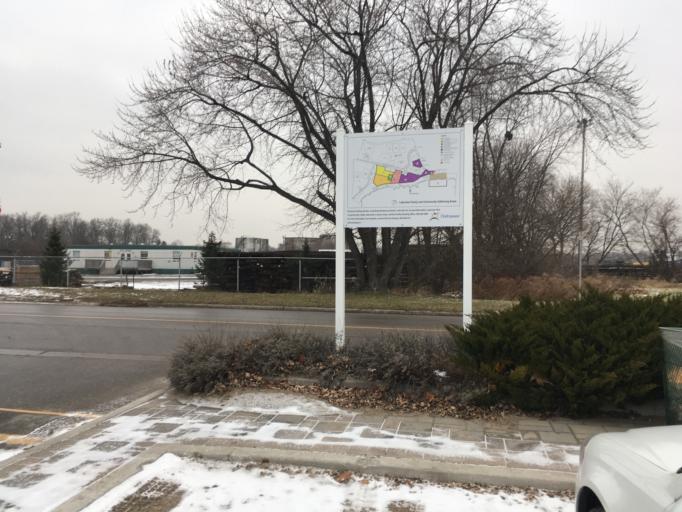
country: CA
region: Ontario
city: Oshawa
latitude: 43.8649
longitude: -78.8257
